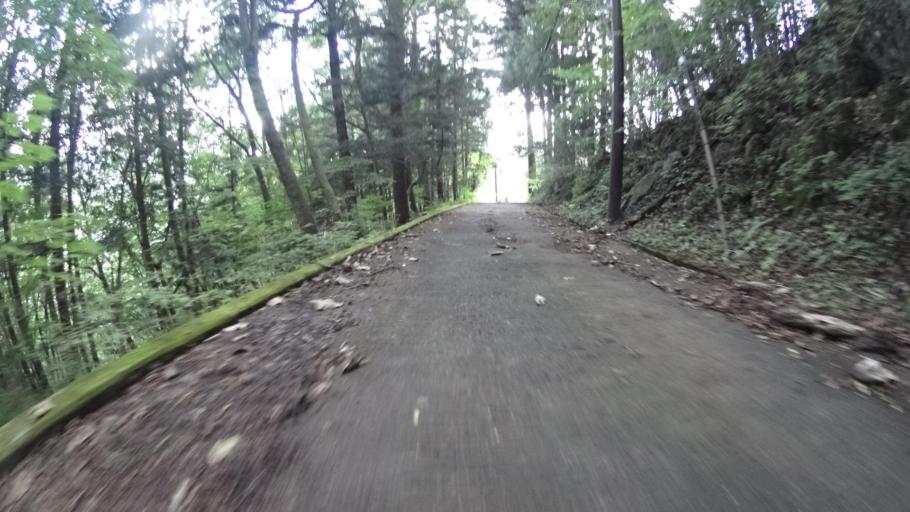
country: JP
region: Yamanashi
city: Uenohara
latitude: 35.7432
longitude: 139.0628
